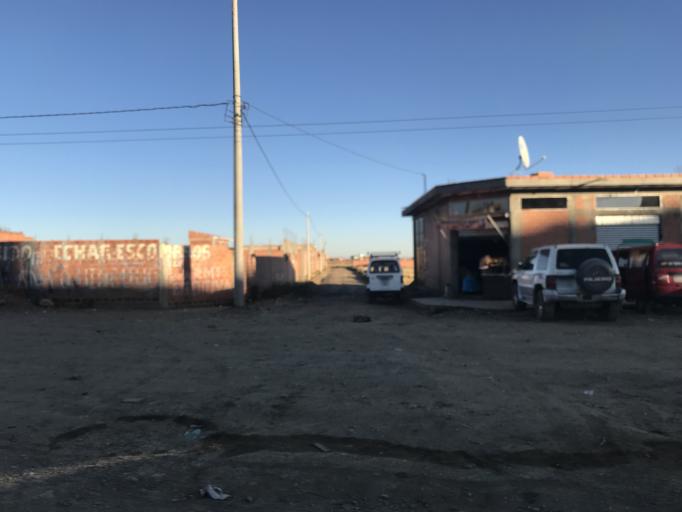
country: BO
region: La Paz
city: La Paz
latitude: -16.5070
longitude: -68.2584
